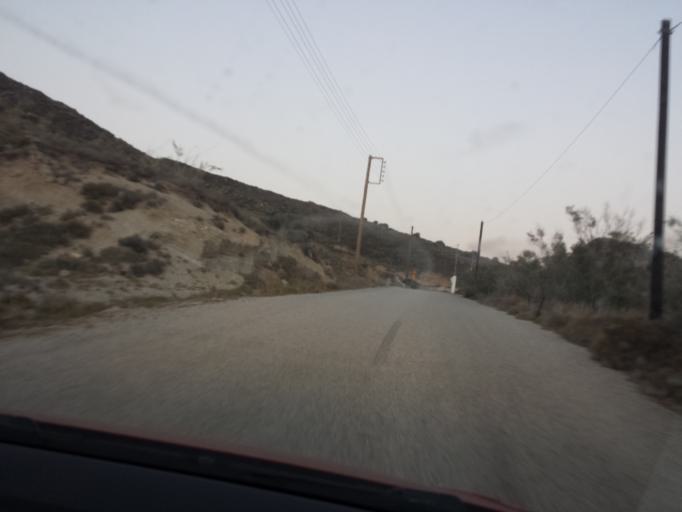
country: GR
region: South Aegean
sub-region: Nomos Kykladon
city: Milos
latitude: 36.7536
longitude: 24.4142
